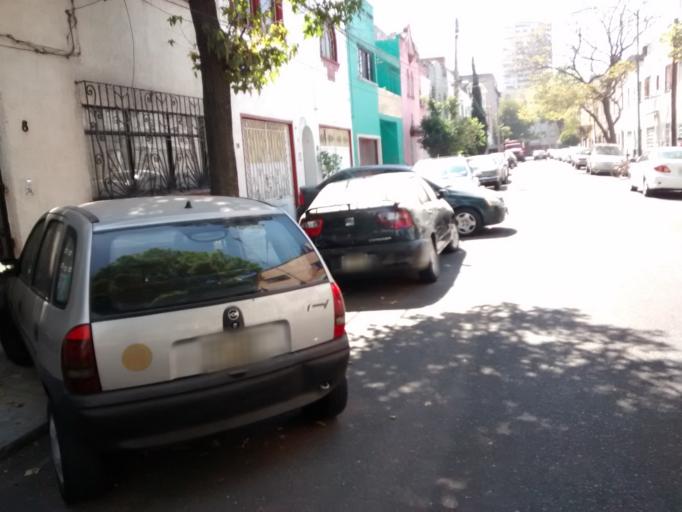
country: MX
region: Mexico City
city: Polanco
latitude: 19.4147
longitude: -99.1785
